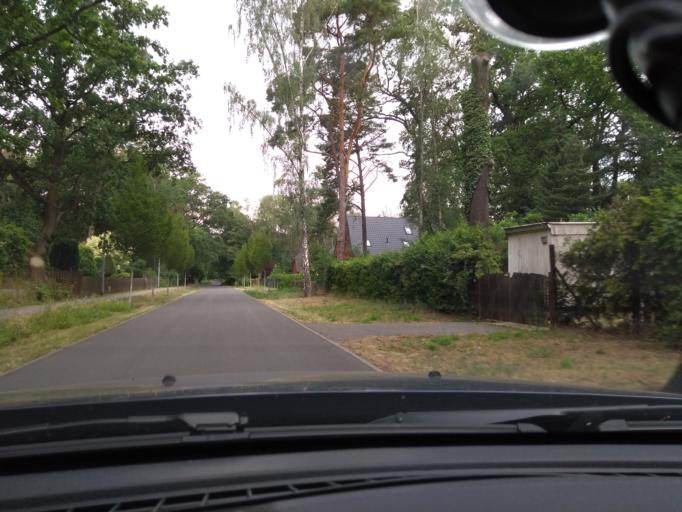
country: DE
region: Brandenburg
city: Dallgow-Doeberitz
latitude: 52.5596
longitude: 13.0620
